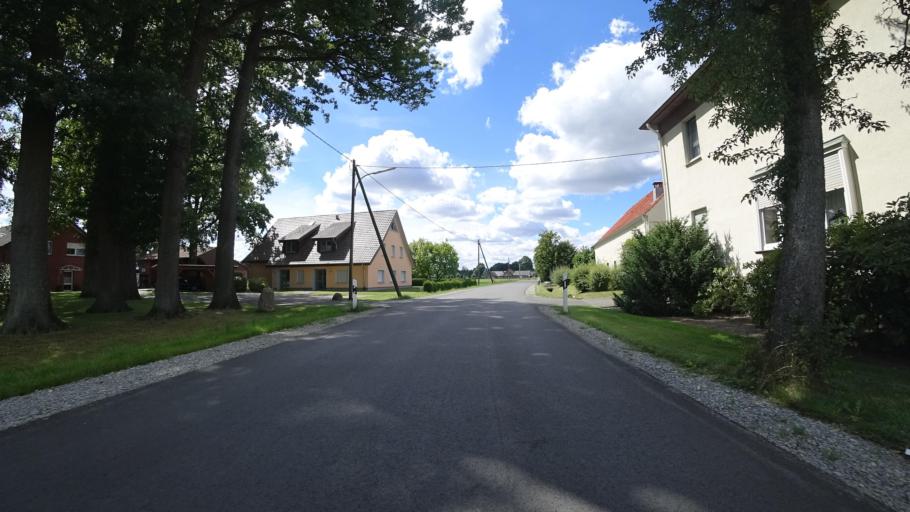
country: DE
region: North Rhine-Westphalia
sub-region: Regierungsbezirk Detmold
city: Steinhagen
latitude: 51.9543
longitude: 8.4188
